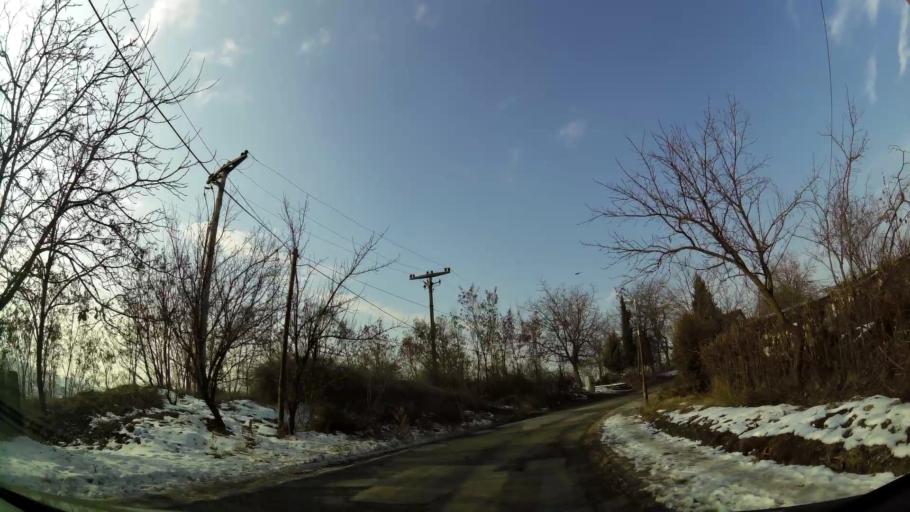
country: MK
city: Creshevo
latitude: 42.0121
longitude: 21.5007
